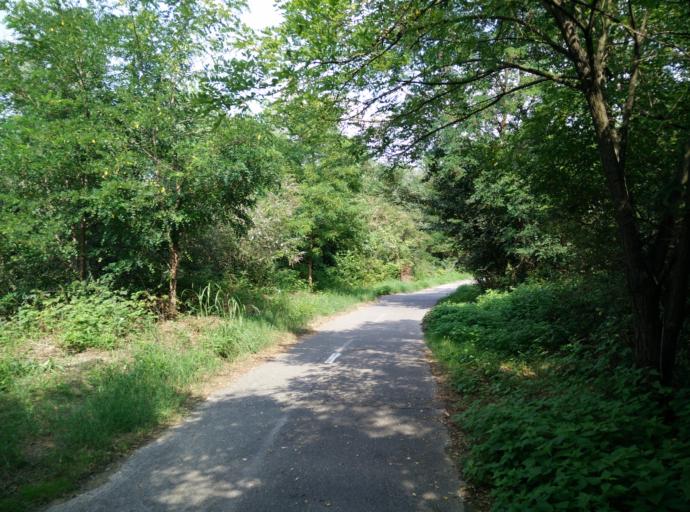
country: IT
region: Piedmont
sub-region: Provincia di Torino
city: Pasta
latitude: 45.0177
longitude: 7.5627
